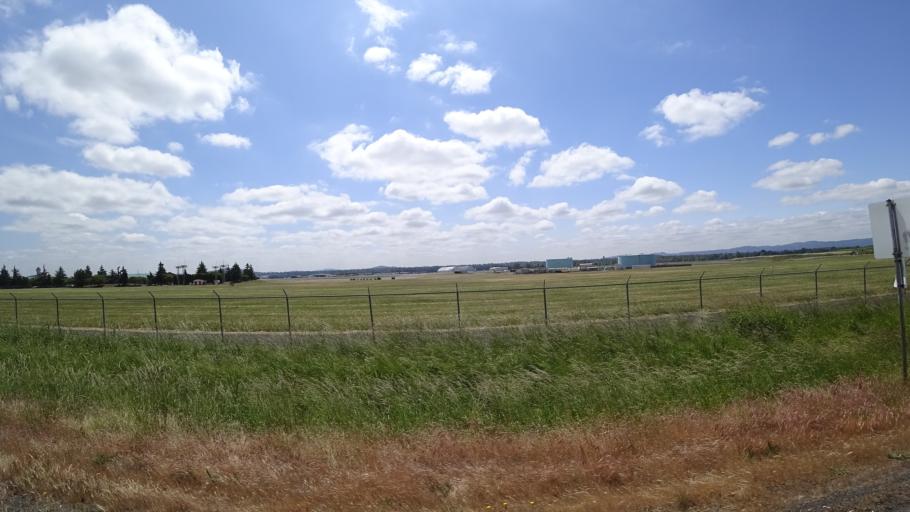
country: US
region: Washington
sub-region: Clark County
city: Vancouver
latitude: 45.5994
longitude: -122.6122
